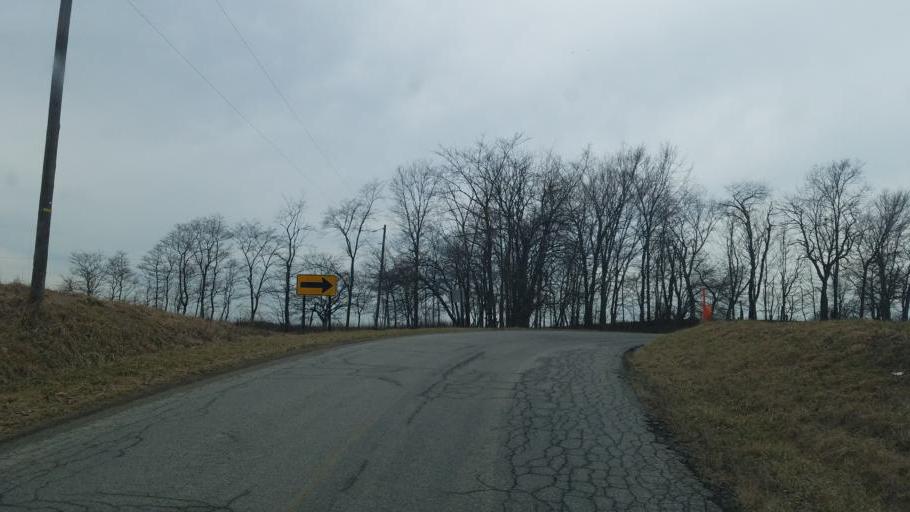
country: US
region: Ohio
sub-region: Richland County
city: Lincoln Heights
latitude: 40.7357
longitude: -82.4253
